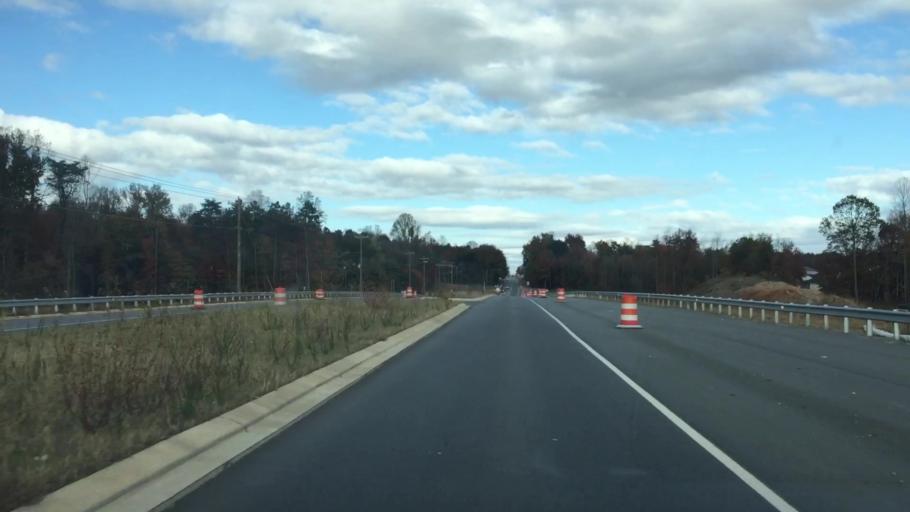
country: US
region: North Carolina
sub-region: Forsyth County
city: Walkertown
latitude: 36.1471
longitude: -80.1553
